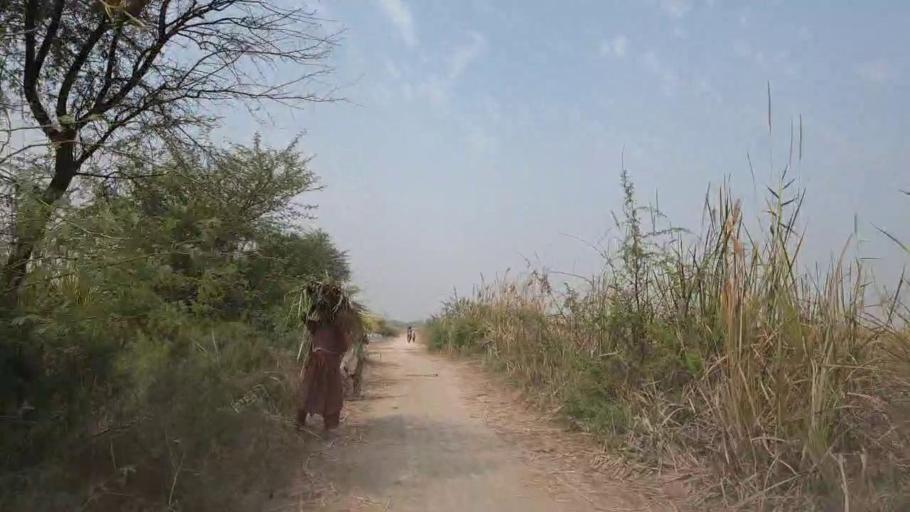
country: PK
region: Sindh
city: Mirpur Khas
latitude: 25.5658
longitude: 69.1047
